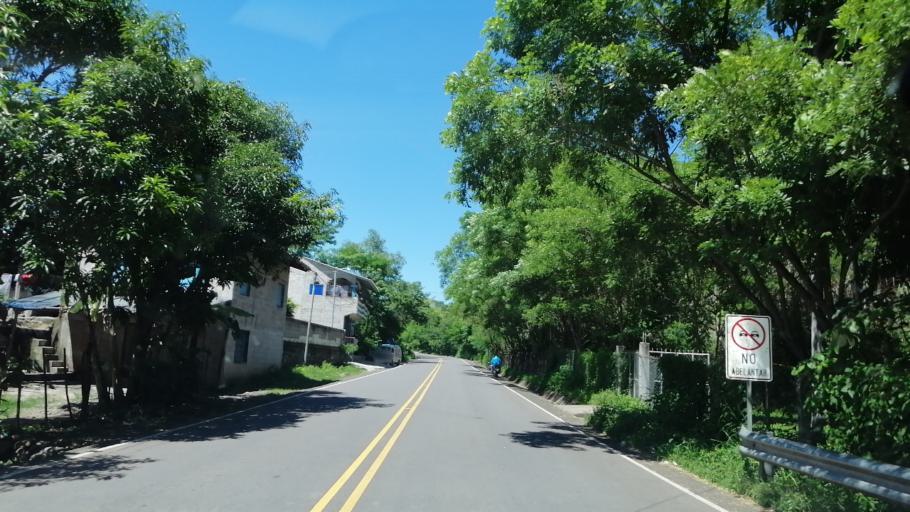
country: SV
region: San Miguel
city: Ciudad Barrios
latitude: 13.8124
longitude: -88.1825
